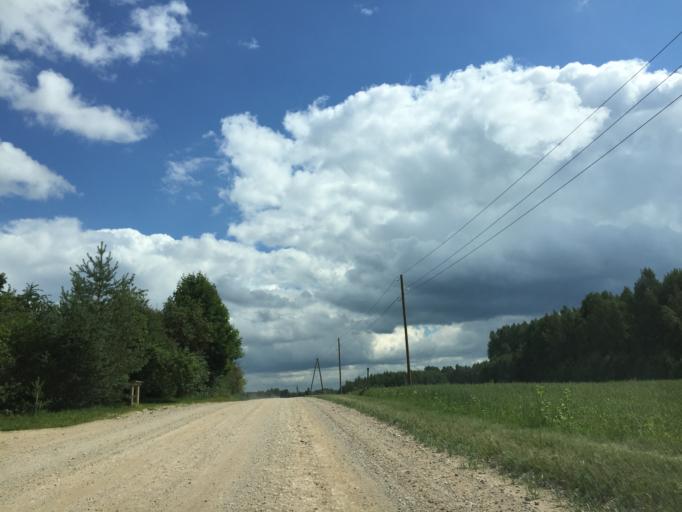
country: LV
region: Malpils
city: Malpils
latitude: 56.8722
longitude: 25.0051
